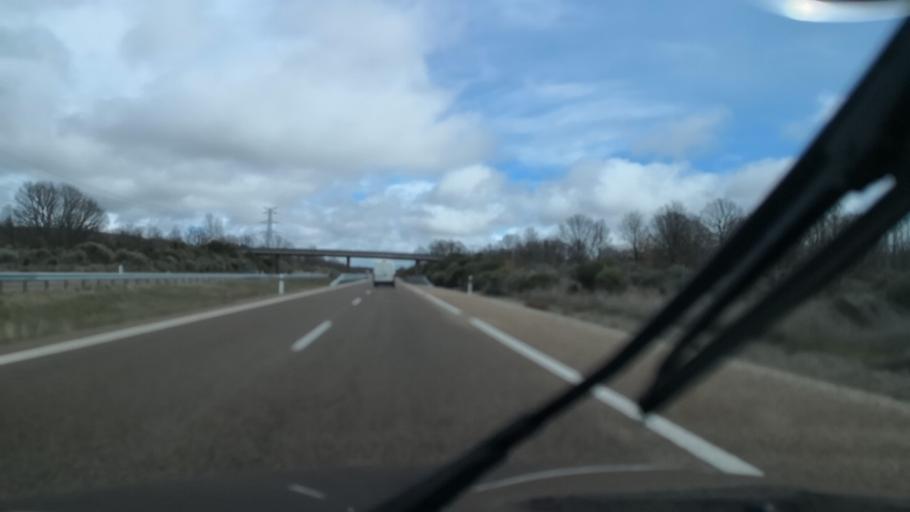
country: ES
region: Castille and Leon
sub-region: Provincia de Zamora
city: Cernadilla
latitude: 42.0227
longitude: -6.3900
